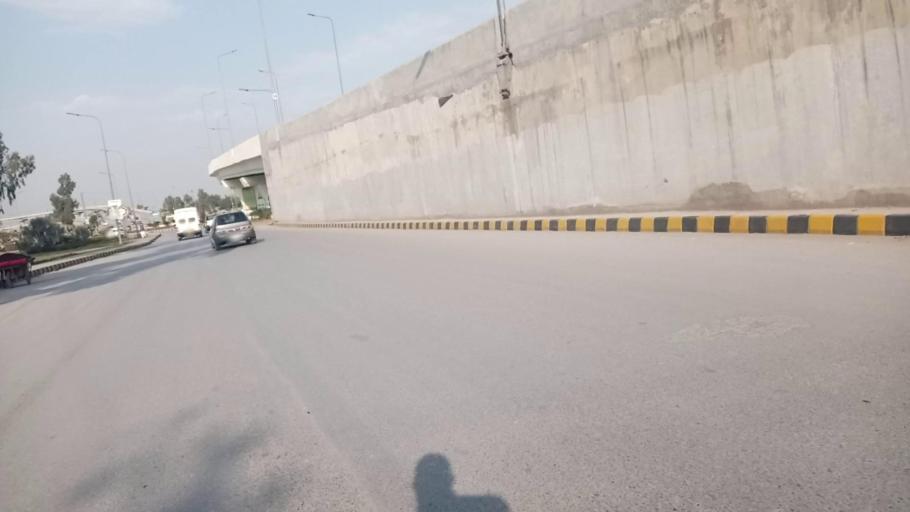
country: PK
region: Khyber Pakhtunkhwa
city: Peshawar
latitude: 33.9913
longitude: 71.4557
